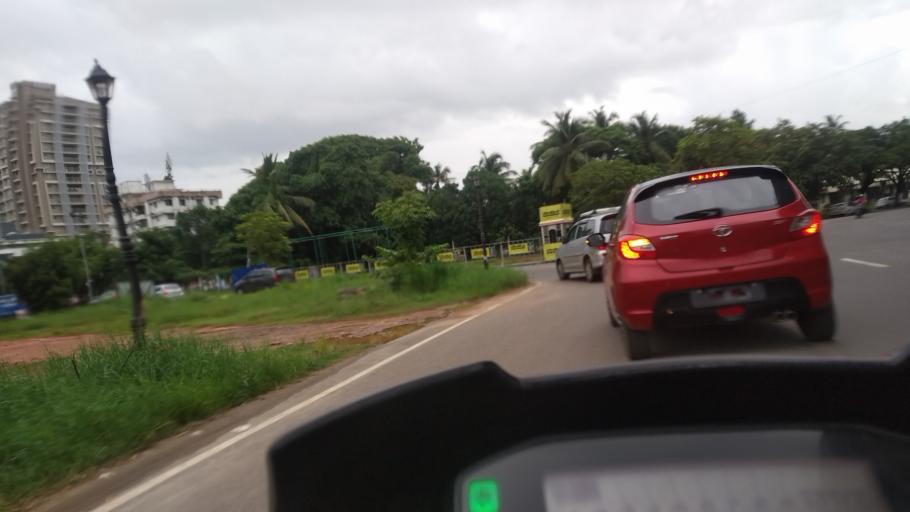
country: IN
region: Kerala
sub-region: Ernakulam
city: Cochin
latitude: 9.9961
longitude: 76.3016
